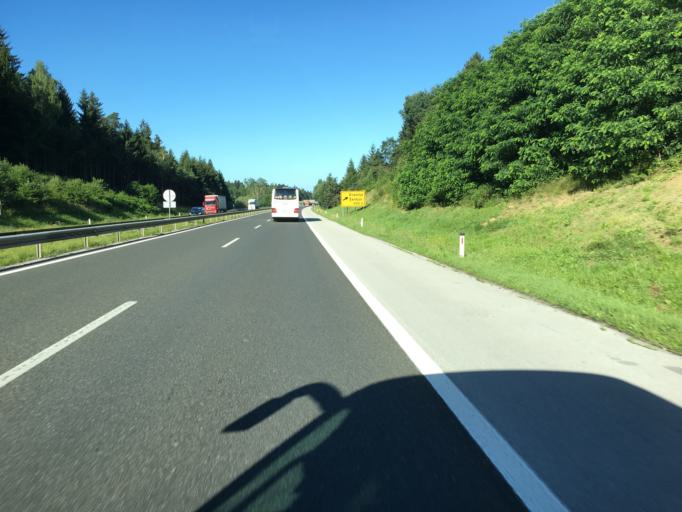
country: SI
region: Sentjur pri Celju
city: Sentjur
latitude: 46.2670
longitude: 15.4016
